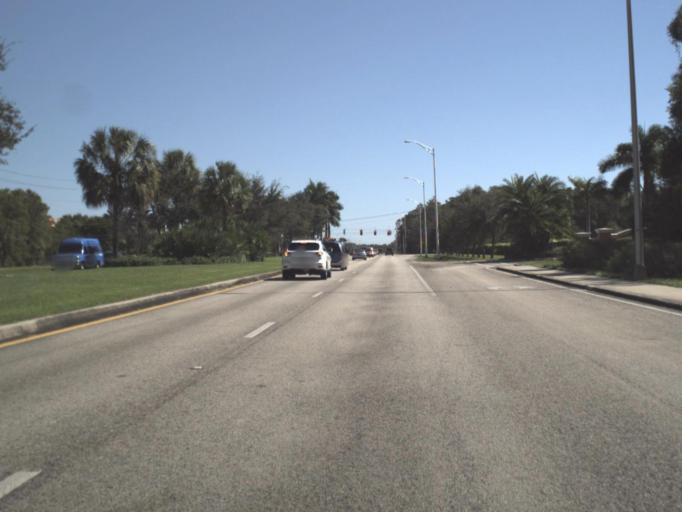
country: US
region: Florida
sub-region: Collier County
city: Lely
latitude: 26.1387
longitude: -81.7331
